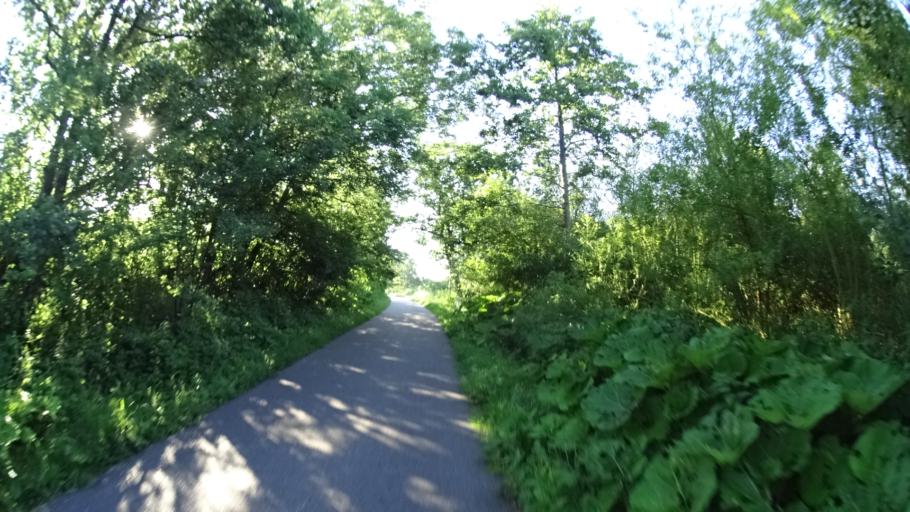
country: DK
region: Central Jutland
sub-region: Arhus Kommune
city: Stavtrup
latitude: 56.1439
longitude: 10.1599
